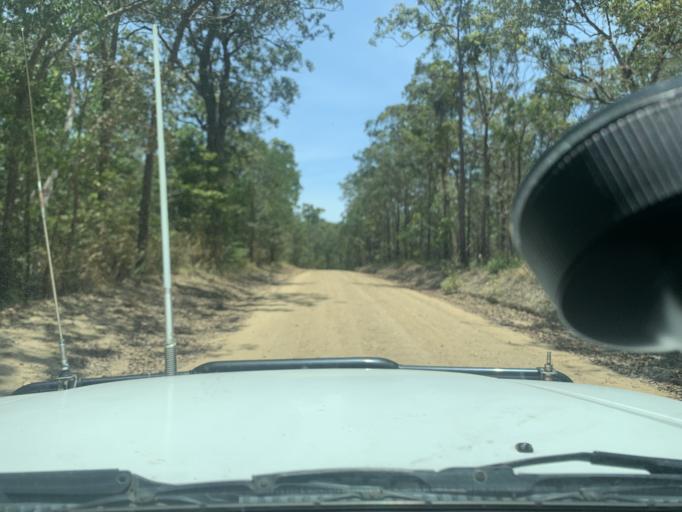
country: AU
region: Queensland
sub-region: Tablelands
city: Kuranda
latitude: -16.9205
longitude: 145.5909
